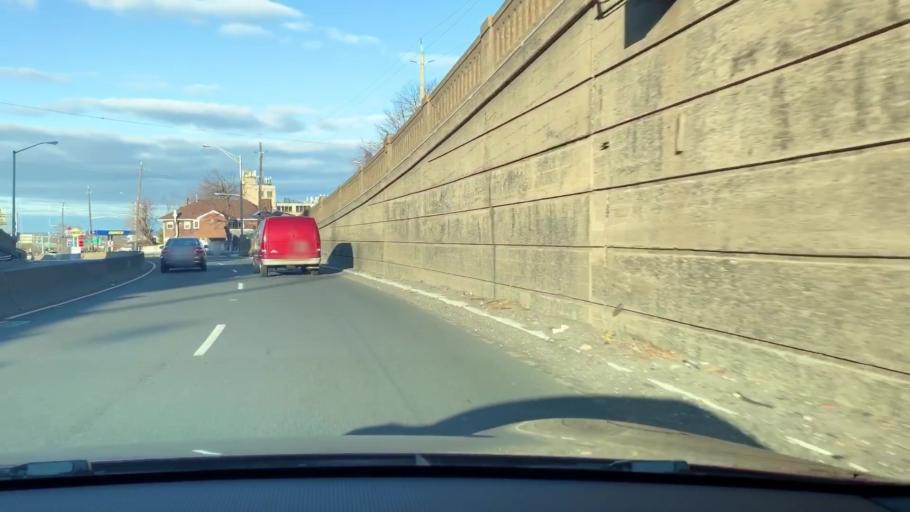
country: US
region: New Jersey
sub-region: Bergen County
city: Palisades Park
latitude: 40.8434
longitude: -74.0022
